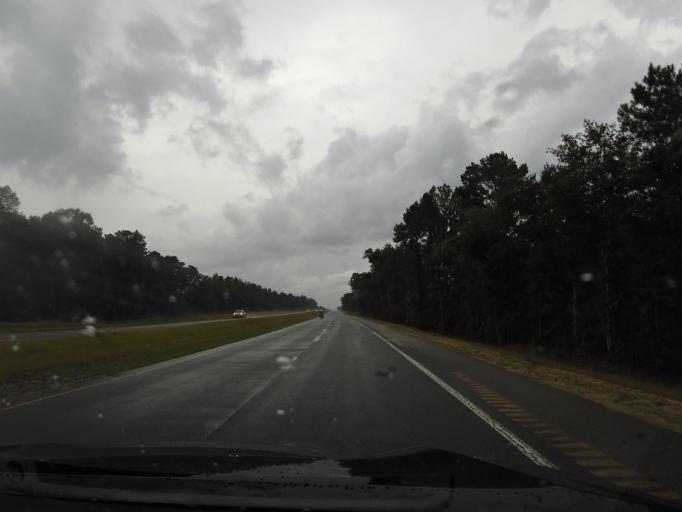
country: US
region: Georgia
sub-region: McIntosh County
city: Darien
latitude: 31.4276
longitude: -81.6714
